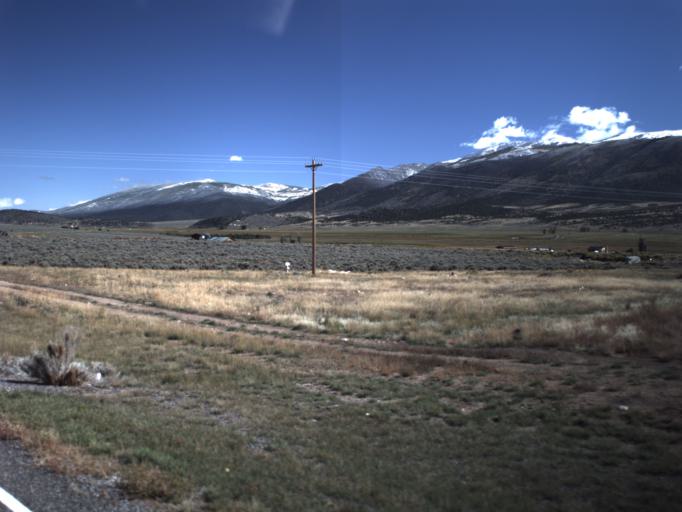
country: US
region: Utah
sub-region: Sevier County
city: Monroe
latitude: 38.5215
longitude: -111.8812
